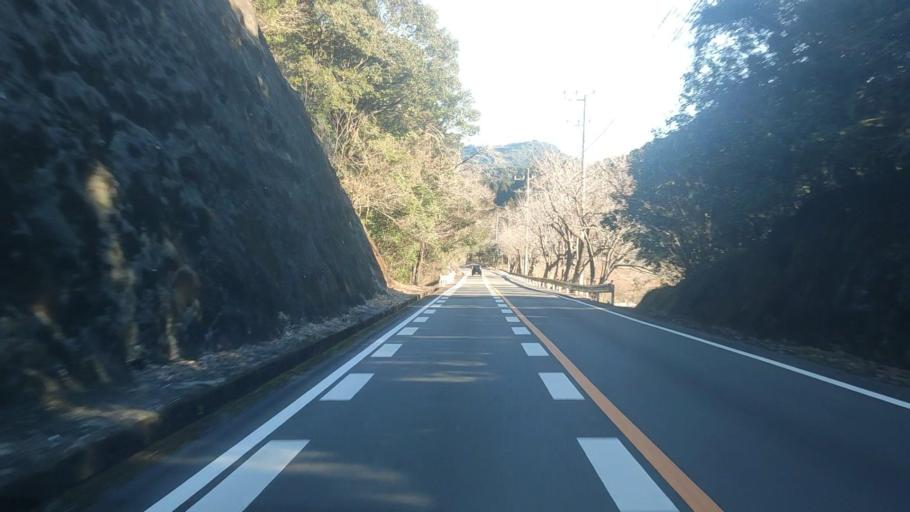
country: JP
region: Miyazaki
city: Nobeoka
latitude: 32.6368
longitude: 131.7415
